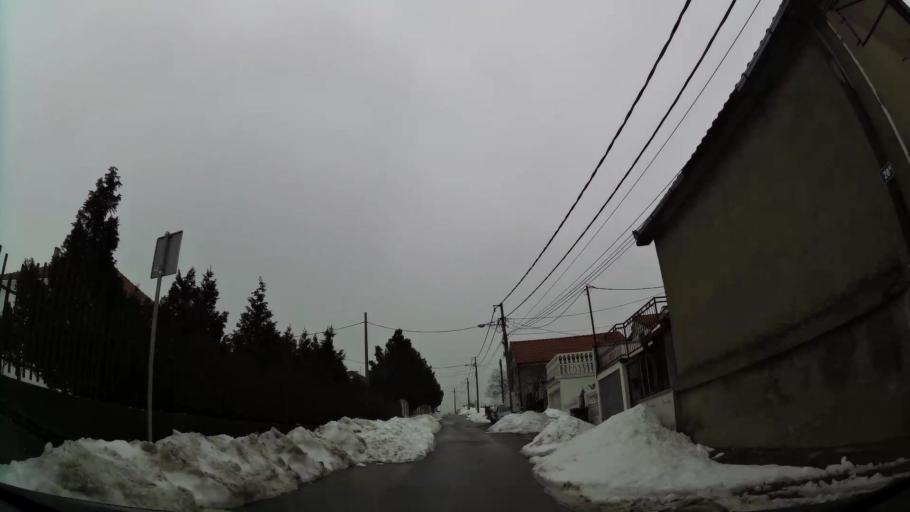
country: RS
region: Central Serbia
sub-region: Belgrade
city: Zvezdara
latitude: 44.7538
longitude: 20.5181
